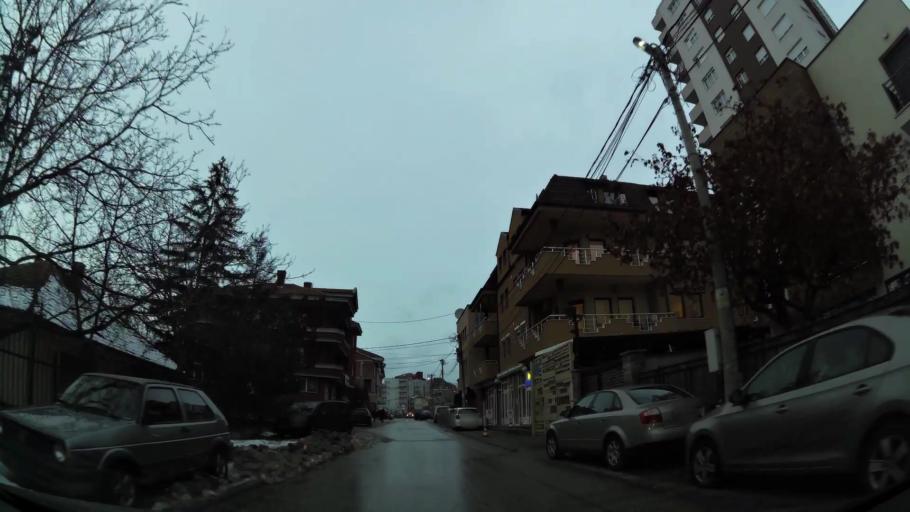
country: XK
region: Pristina
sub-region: Komuna e Prishtines
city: Pristina
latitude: 42.6579
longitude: 21.1663
